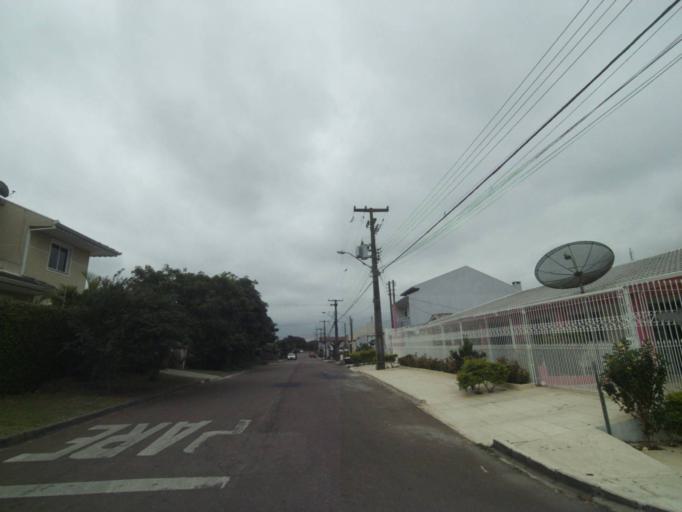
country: BR
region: Parana
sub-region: Sao Jose Dos Pinhais
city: Sao Jose dos Pinhais
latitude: -25.5456
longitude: -49.2546
